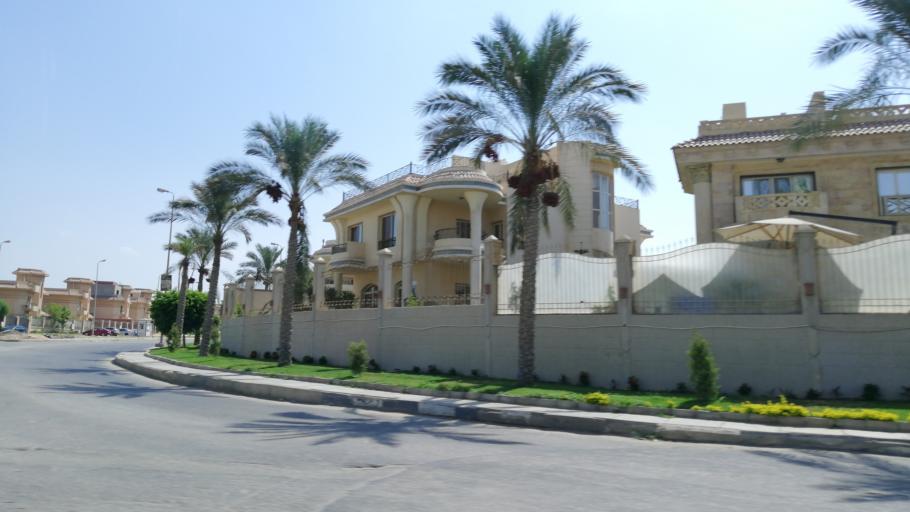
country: EG
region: Muhafazat al Qalyubiyah
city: Al Khankah
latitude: 30.0537
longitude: 31.4850
